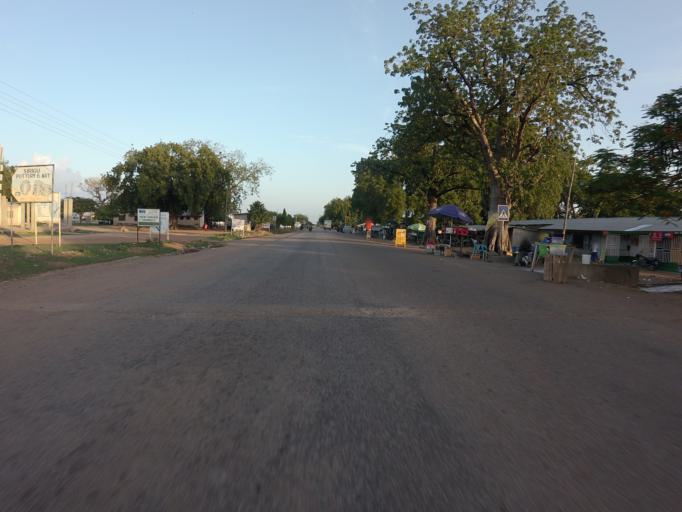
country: GH
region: Upper East
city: Navrongo
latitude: 10.9700
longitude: -1.1024
